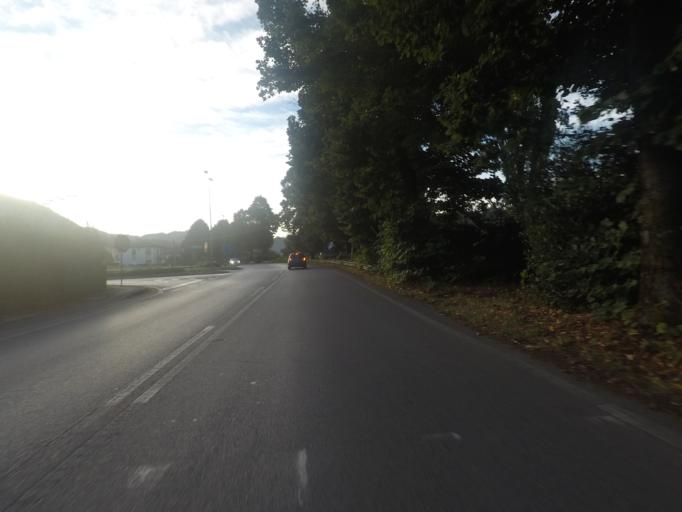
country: IT
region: Tuscany
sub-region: Provincia di Lucca
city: Corsanico-Bargecchia
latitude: 43.9285
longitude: 10.3145
